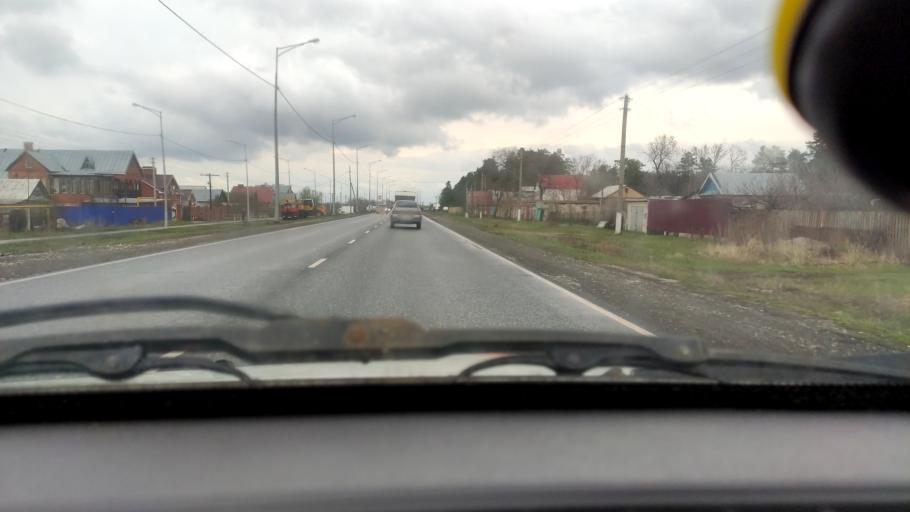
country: RU
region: Samara
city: Povolzhskiy
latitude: 53.5895
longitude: 49.5775
